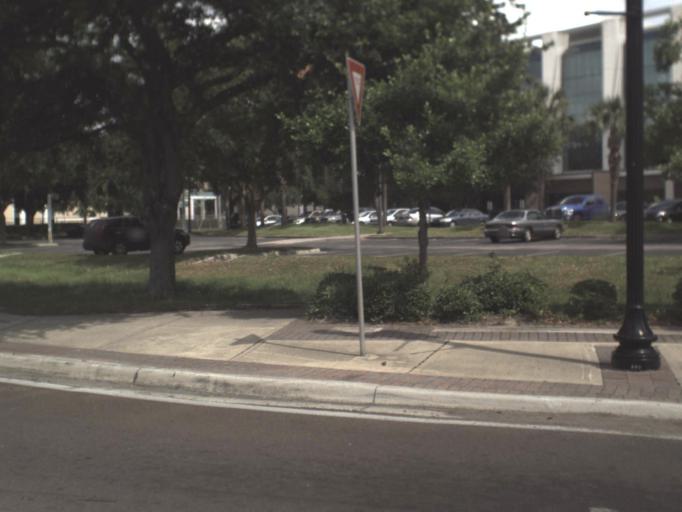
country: US
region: Florida
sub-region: Duval County
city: Jacksonville
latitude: 30.3347
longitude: -81.6635
